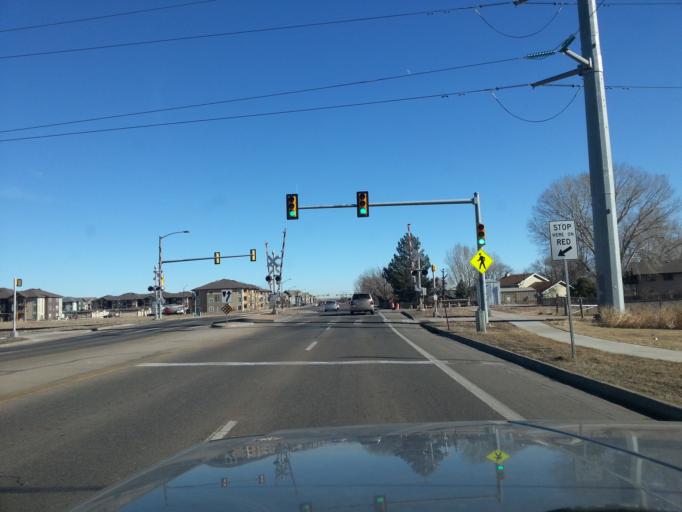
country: US
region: Colorado
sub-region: Larimer County
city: Fort Collins
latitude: 40.5526
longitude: -105.0440
